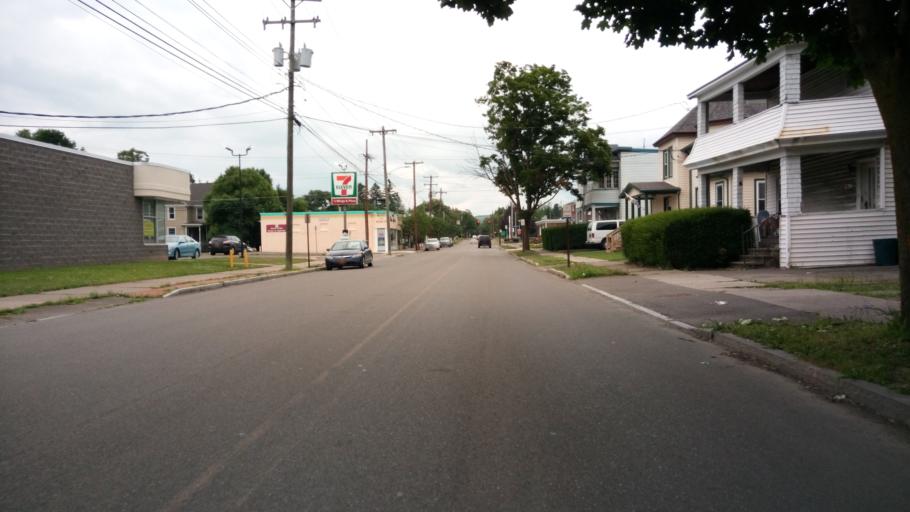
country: US
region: New York
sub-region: Chemung County
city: Elmira
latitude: 42.0841
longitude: -76.8218
